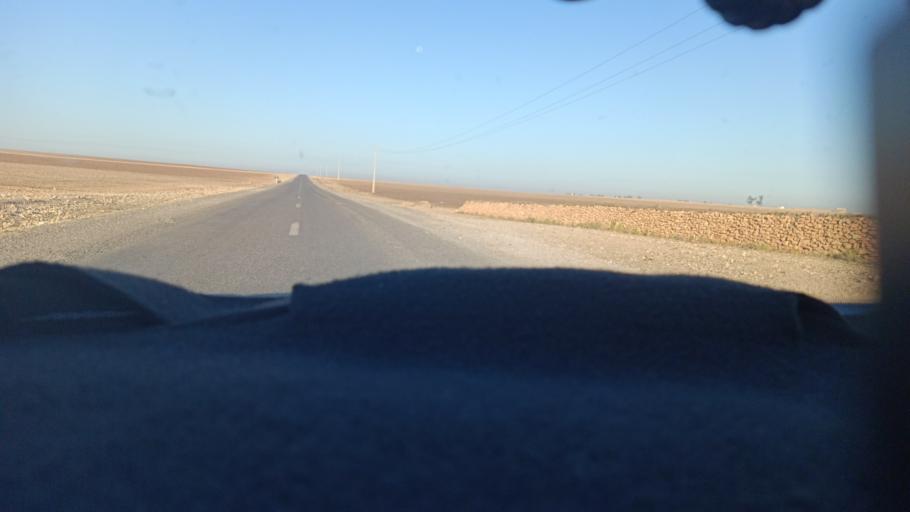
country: MA
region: Doukkala-Abda
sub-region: Safi
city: Youssoufia
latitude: 32.3719
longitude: -8.6337
